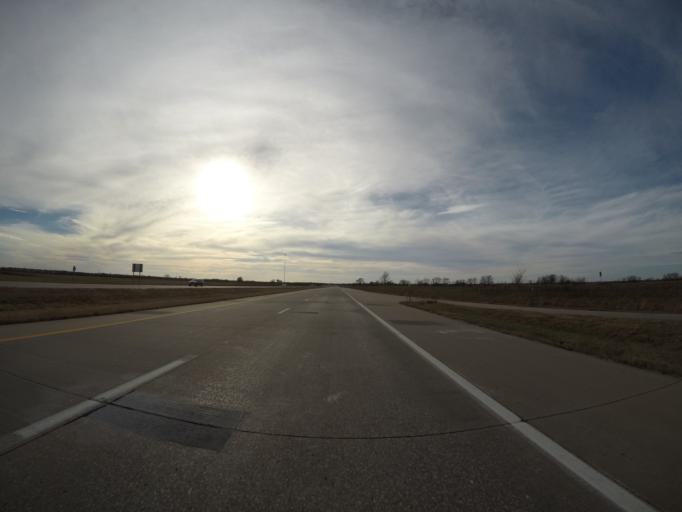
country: US
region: Kansas
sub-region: Franklin County
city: Wellsville
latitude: 38.6693
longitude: -95.1587
